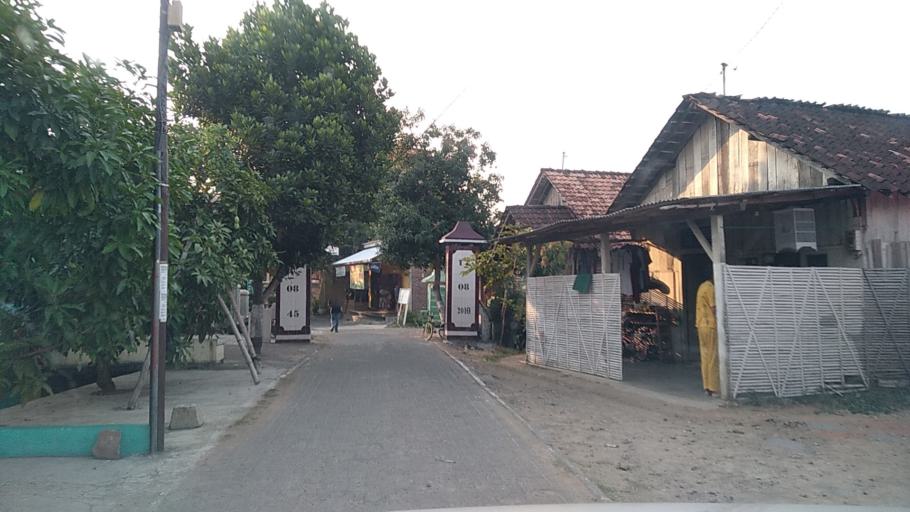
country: ID
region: Central Java
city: Semarang
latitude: -6.9698
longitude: 110.2965
